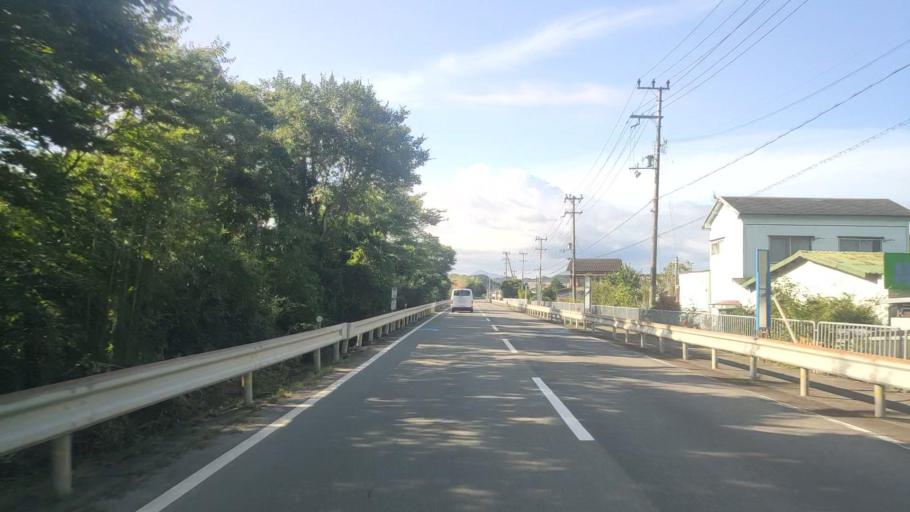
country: JP
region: Wakayama
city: Tanabe
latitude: 33.6704
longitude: 135.4080
